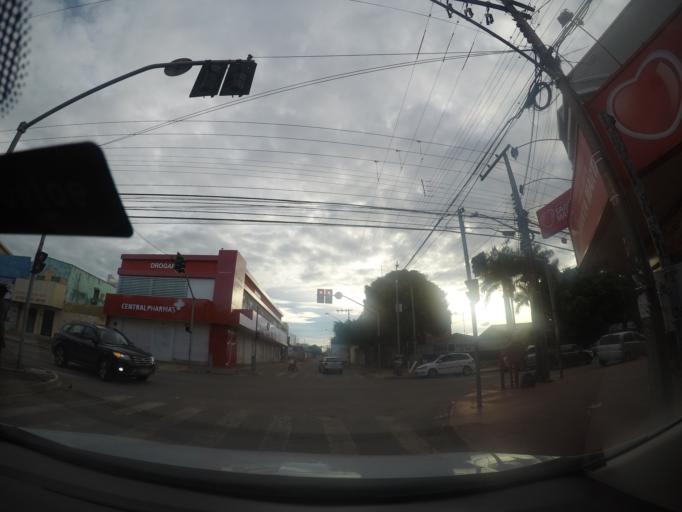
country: BR
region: Goias
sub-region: Goiania
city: Goiania
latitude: -16.6448
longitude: -49.3250
